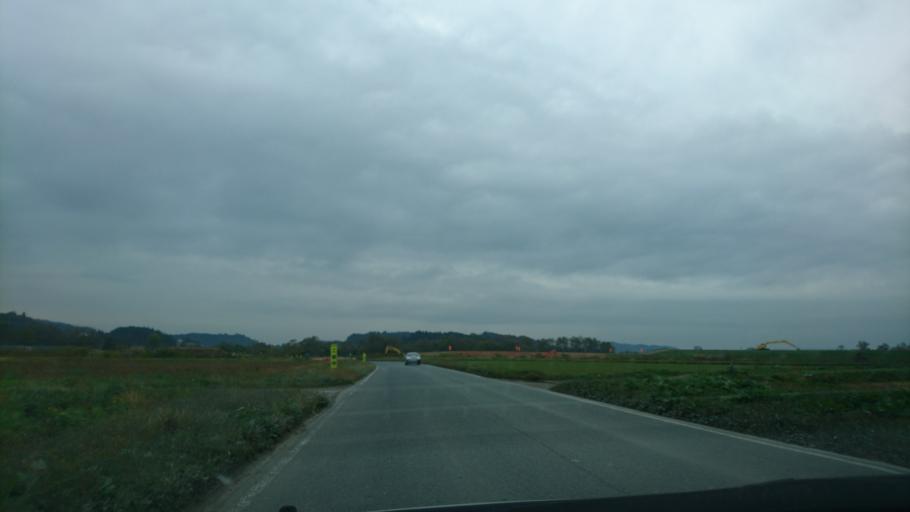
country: JP
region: Iwate
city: Ichinoseki
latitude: 38.9533
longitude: 141.1689
